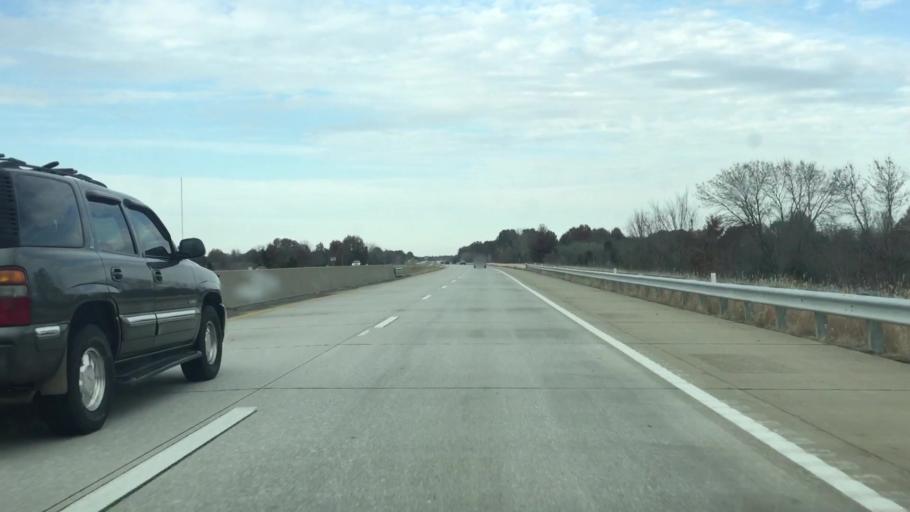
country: US
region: Missouri
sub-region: Henry County
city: Clinton
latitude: 38.3317
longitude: -93.7574
